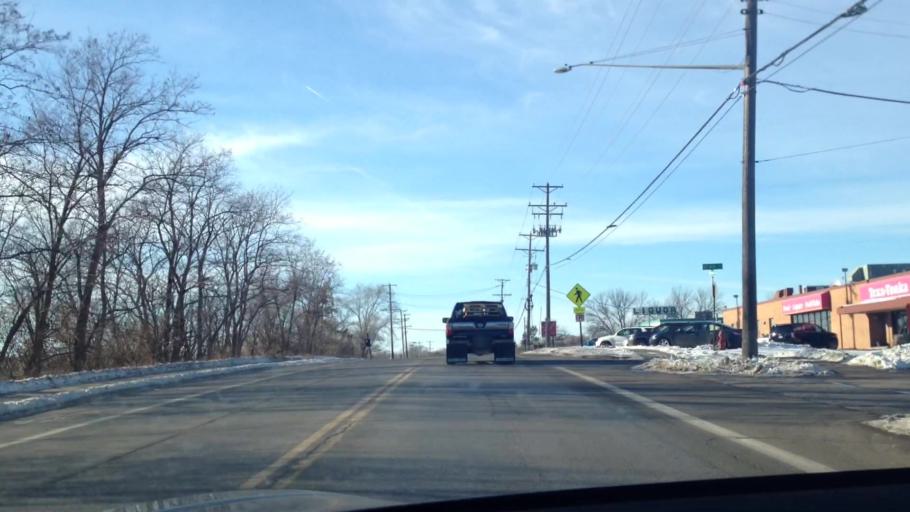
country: US
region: Minnesota
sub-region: Hennepin County
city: Saint Louis Park
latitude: 44.9495
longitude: -93.3833
